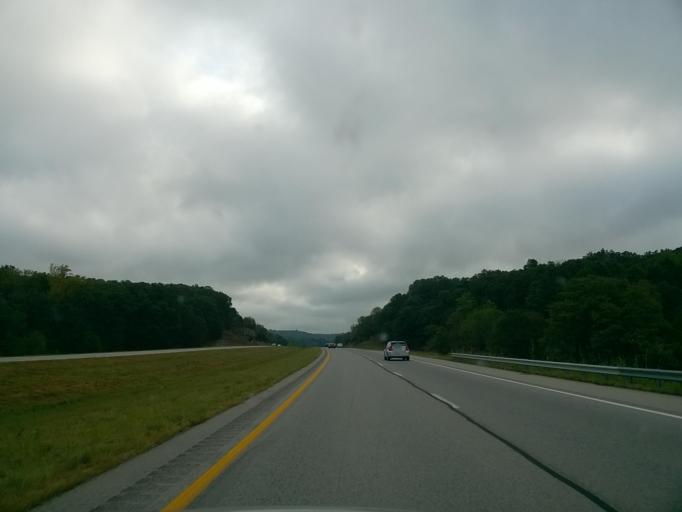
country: US
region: Indiana
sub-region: Crawford County
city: English
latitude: 38.2520
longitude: -86.3212
